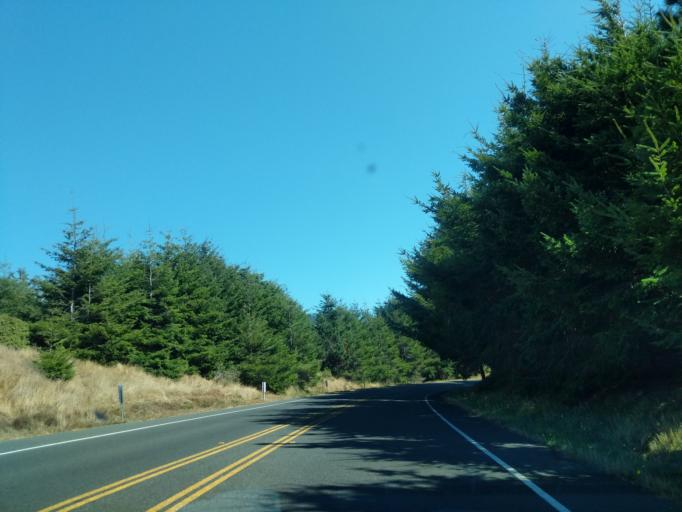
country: US
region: California
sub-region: Sonoma County
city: Monte Rio
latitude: 38.5181
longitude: -123.2447
